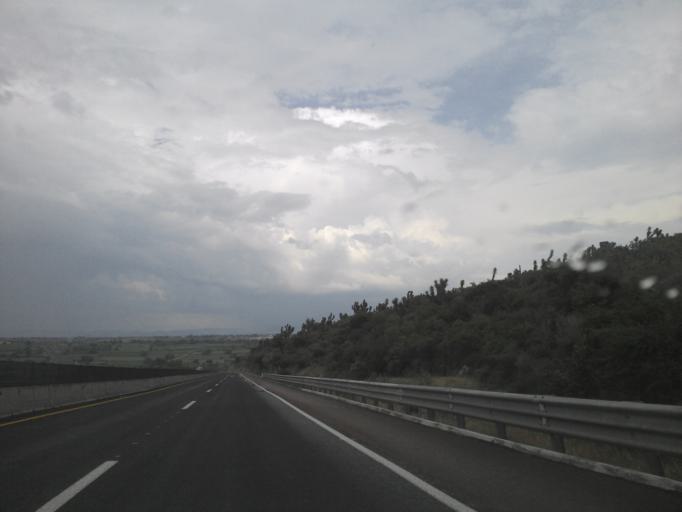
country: MX
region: Hidalgo
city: San Marcos
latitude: 20.0743
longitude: -99.3578
